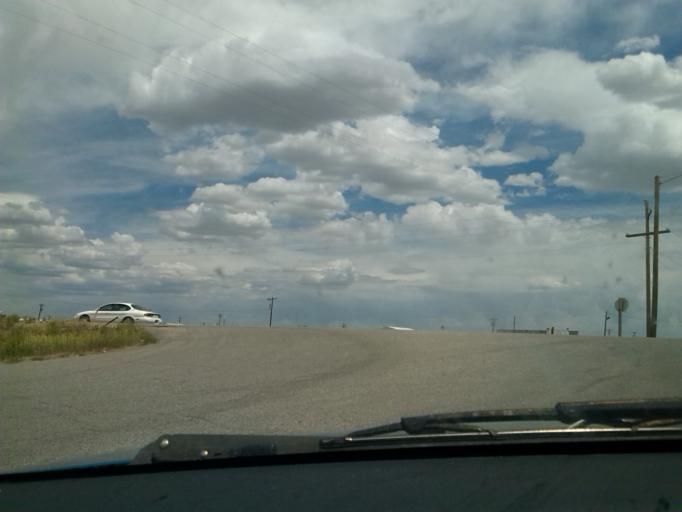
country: US
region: Wyoming
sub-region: Carbon County
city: Rawlins
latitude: 41.7952
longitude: -107.2155
